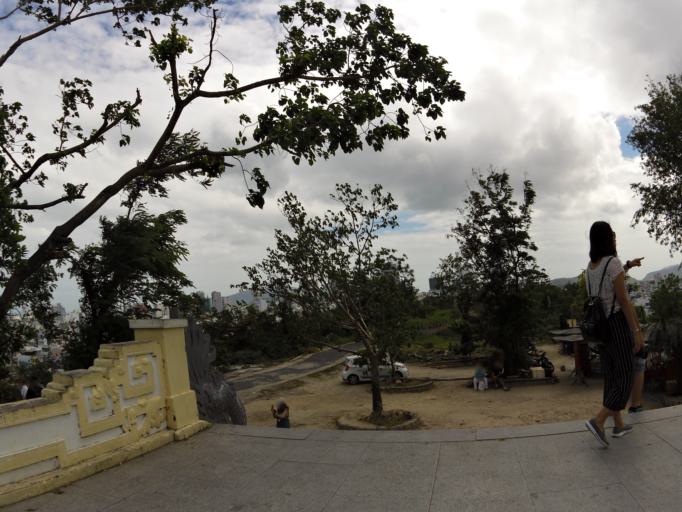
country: VN
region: Khanh Hoa
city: Nha Trang
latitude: 12.2519
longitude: 109.1811
